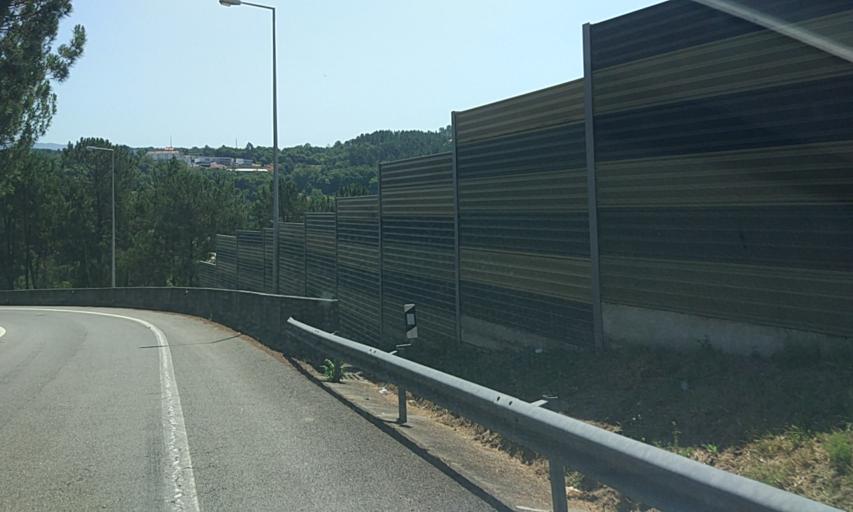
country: PT
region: Porto
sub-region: Amarante
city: Amarante
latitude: 41.2618
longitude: -8.1124
